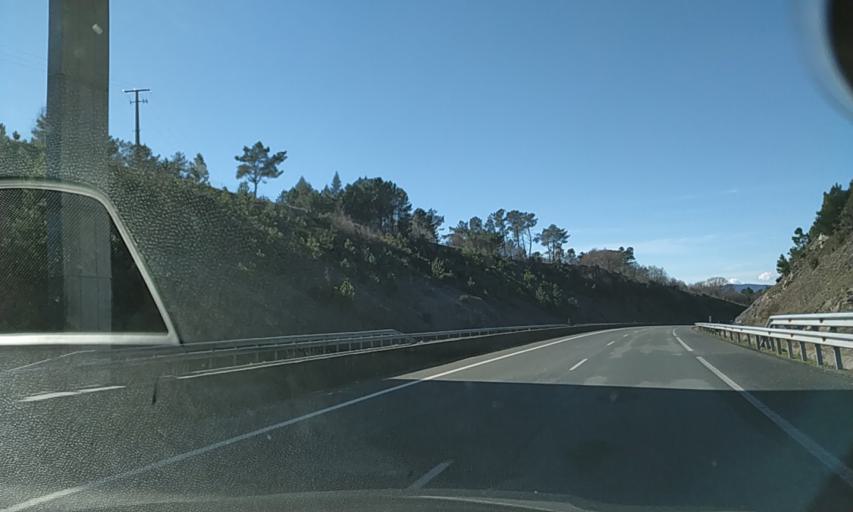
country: ES
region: Galicia
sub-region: Provincia de Pontevedra
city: Lalin
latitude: 42.6249
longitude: -8.1095
